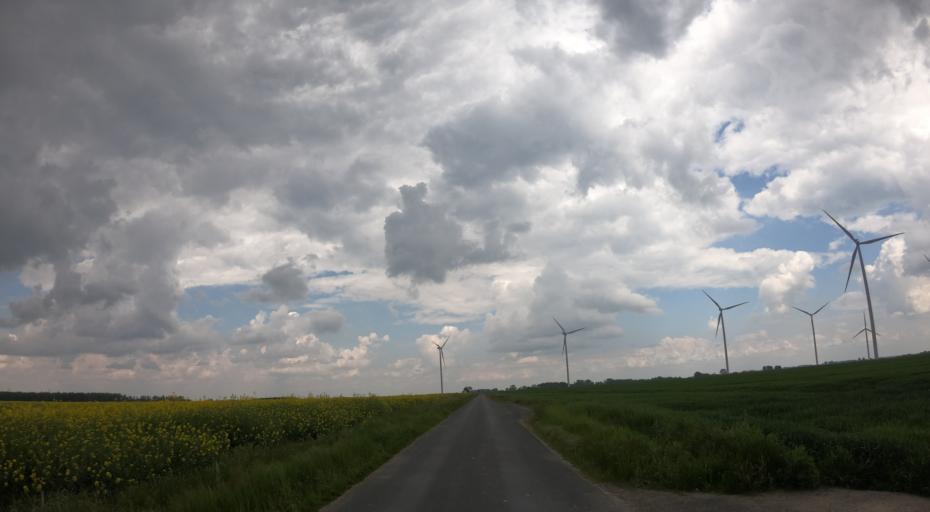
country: PL
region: West Pomeranian Voivodeship
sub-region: Powiat pyrzycki
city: Kozielice
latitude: 53.1444
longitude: 14.7694
